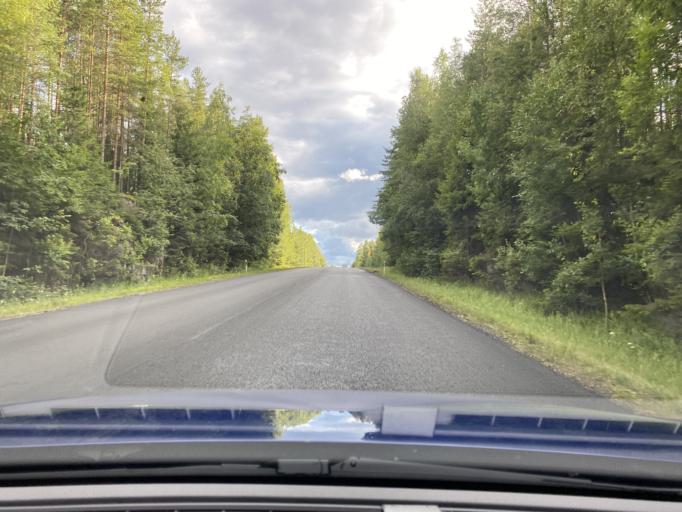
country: FI
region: Haeme
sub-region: Haemeenlinna
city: Renko
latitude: 60.9373
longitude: 24.3754
